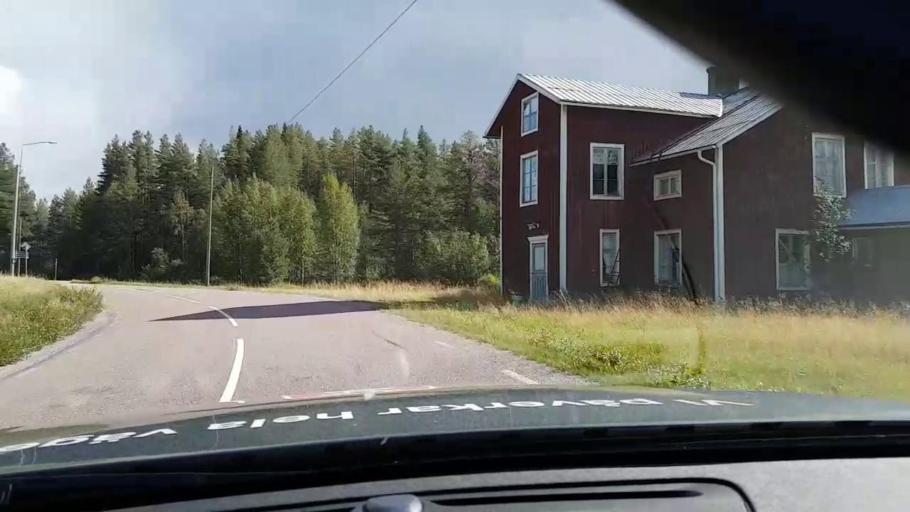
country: SE
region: Vaesterbotten
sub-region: Asele Kommun
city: Asele
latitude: 63.8608
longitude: 17.3730
